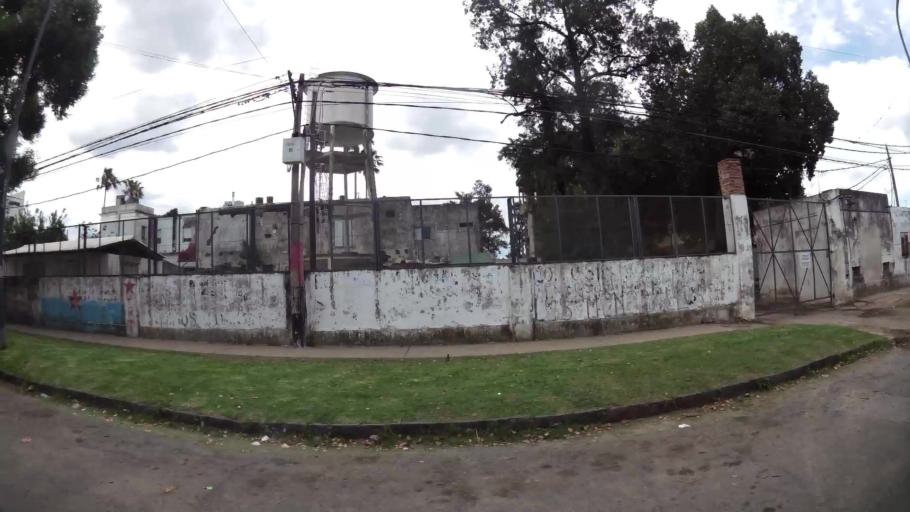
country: AR
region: Santa Fe
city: Gobernador Galvez
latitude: -32.9998
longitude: -60.6465
